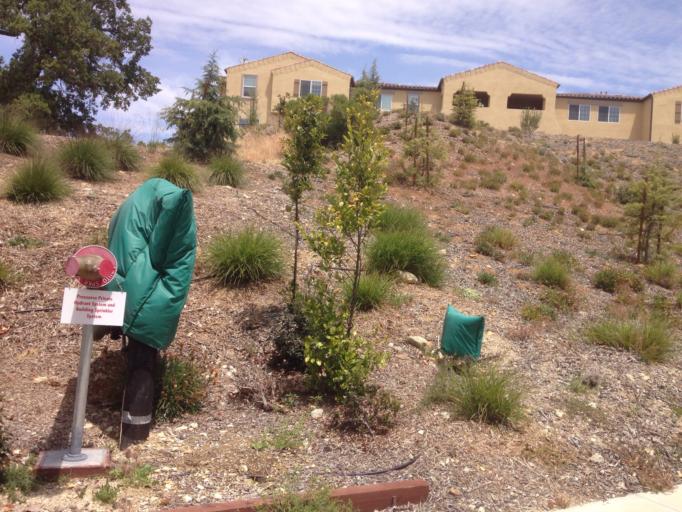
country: US
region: California
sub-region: San Luis Obispo County
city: Atascadero
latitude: 35.4551
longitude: -120.6314
